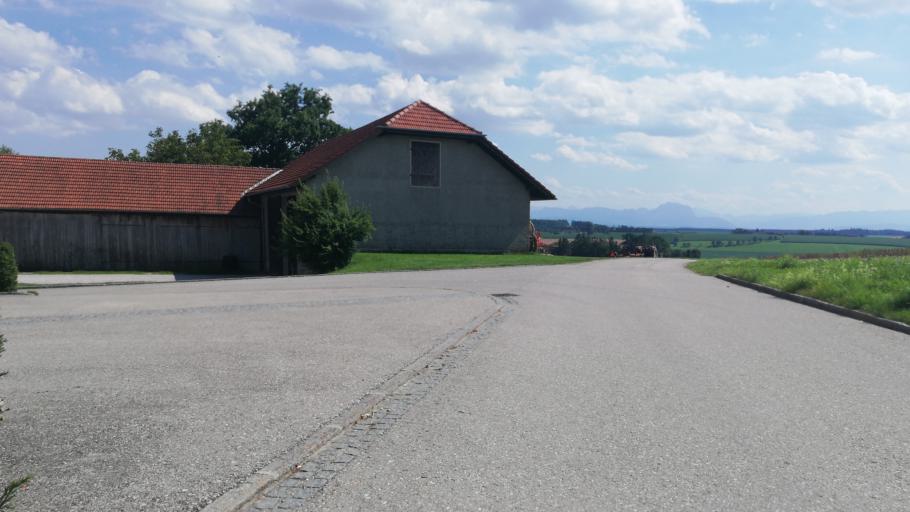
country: AT
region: Upper Austria
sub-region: Wels-Land
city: Pennewang
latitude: 48.1624
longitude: 13.8825
